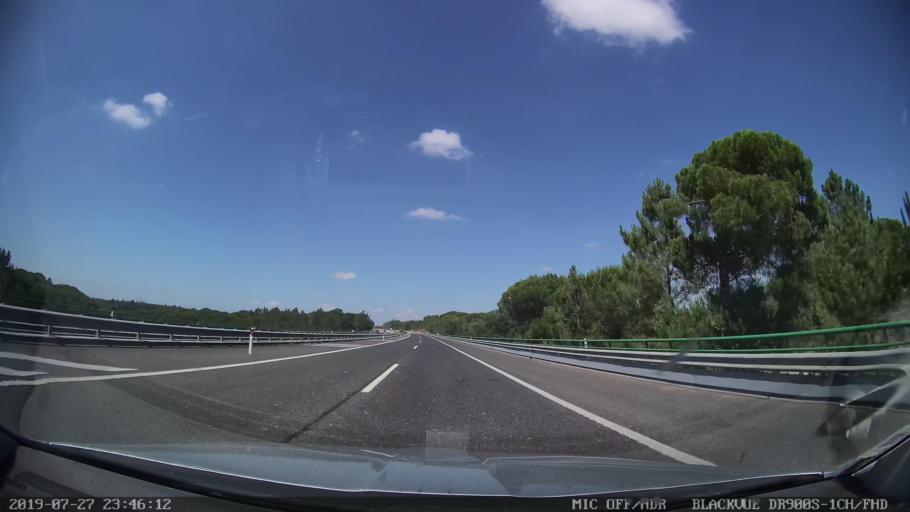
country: PT
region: Evora
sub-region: Vendas Novas
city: Vendas Novas
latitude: 38.6356
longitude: -8.4986
